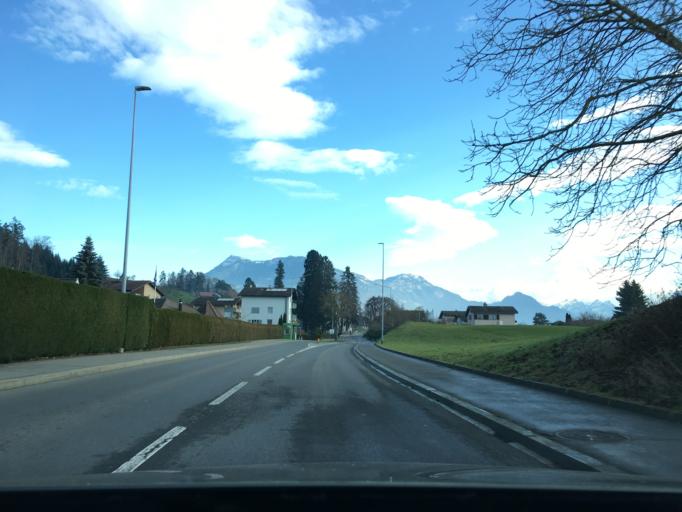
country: CH
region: Lucerne
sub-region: Lucerne-Land District
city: Adligenswil
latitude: 47.0511
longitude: 8.3569
